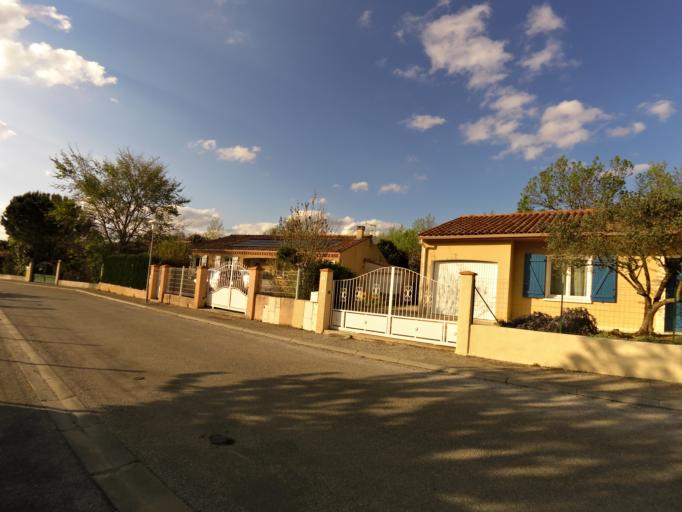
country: FR
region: Midi-Pyrenees
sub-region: Departement du Tarn
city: Soreze
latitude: 43.4520
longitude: 2.0626
